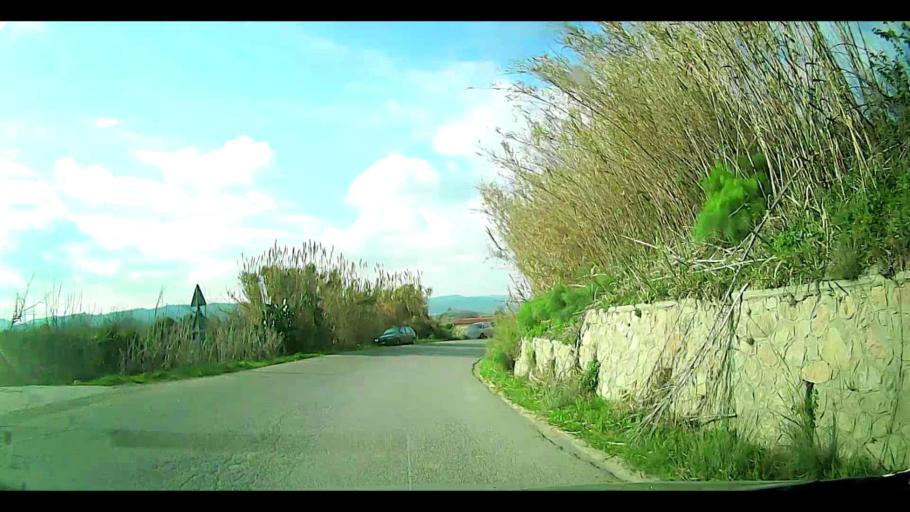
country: IT
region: Calabria
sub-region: Provincia di Crotone
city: Rocca di Neto
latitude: 39.1803
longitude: 17.0357
